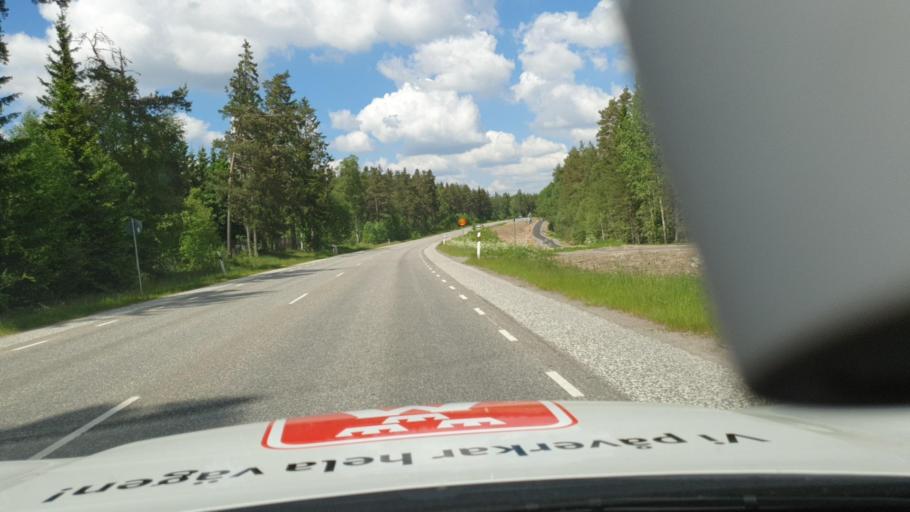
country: SE
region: Joenkoeping
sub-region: Jonkopings Kommun
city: Odensjo
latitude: 57.6588
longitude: 14.1846
